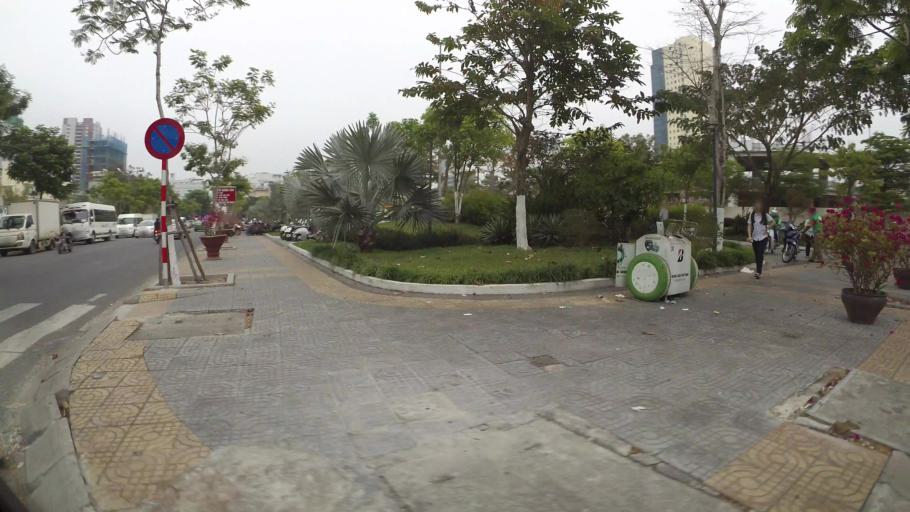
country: VN
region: Da Nang
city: Da Nang
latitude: 16.0684
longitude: 108.2212
